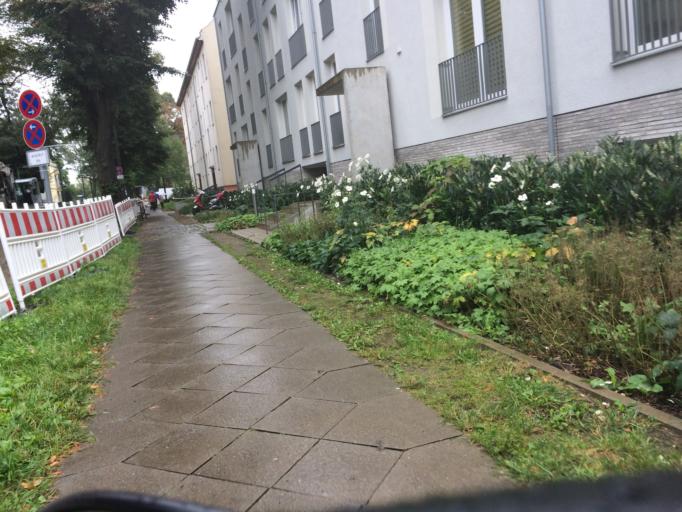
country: DE
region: Berlin
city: Niederschonhausen
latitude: 52.5913
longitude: 13.4087
